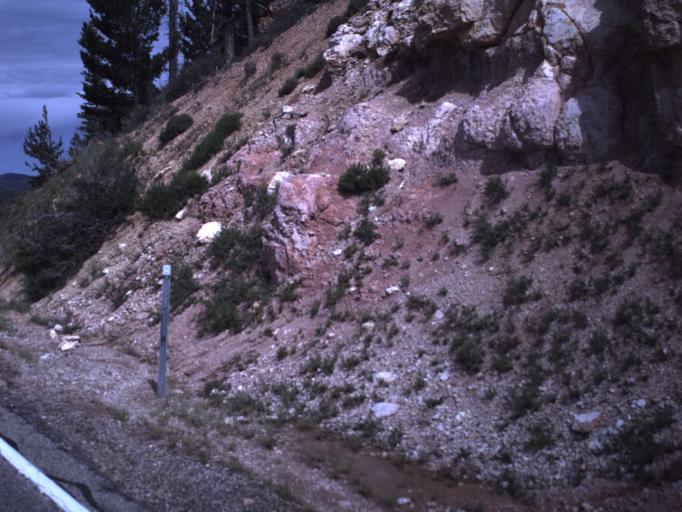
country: US
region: Utah
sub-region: Iron County
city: Cedar City
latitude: 37.5701
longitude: -112.8569
